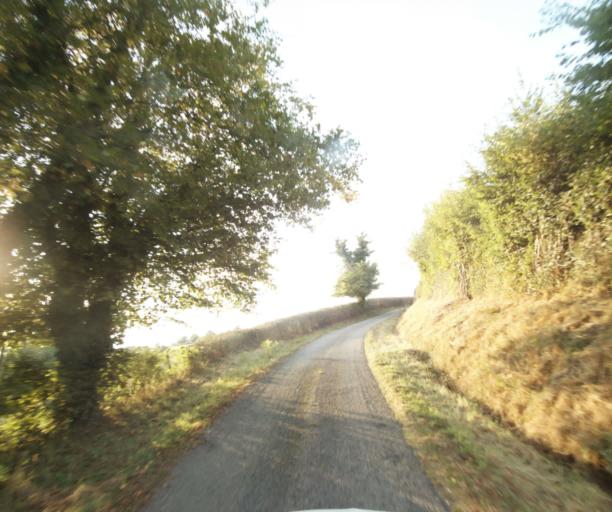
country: FR
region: Bourgogne
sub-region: Departement de Saone-et-Loire
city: Charolles
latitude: 46.4477
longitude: 4.3591
